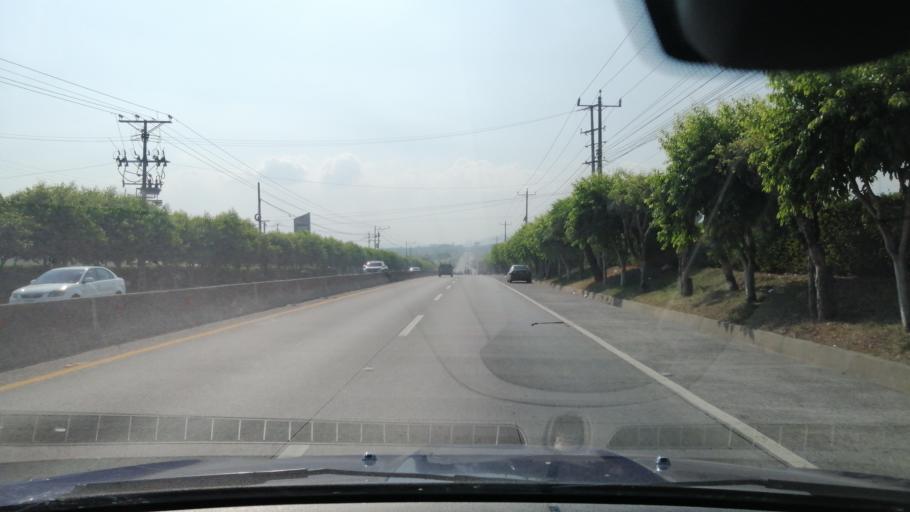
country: SV
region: San Salvador
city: Apopa
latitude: 13.7958
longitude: -89.2274
